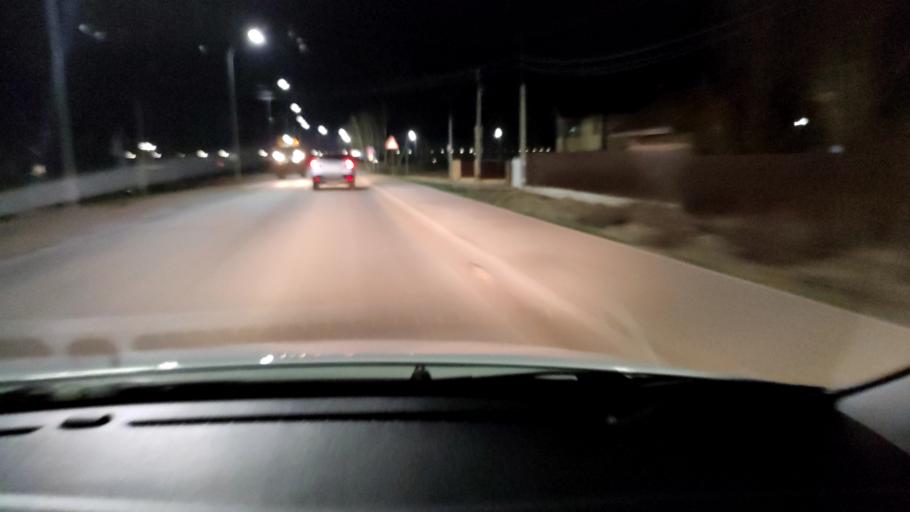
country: RU
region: Tatarstan
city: Stolbishchi
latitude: 55.6936
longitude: 49.2133
